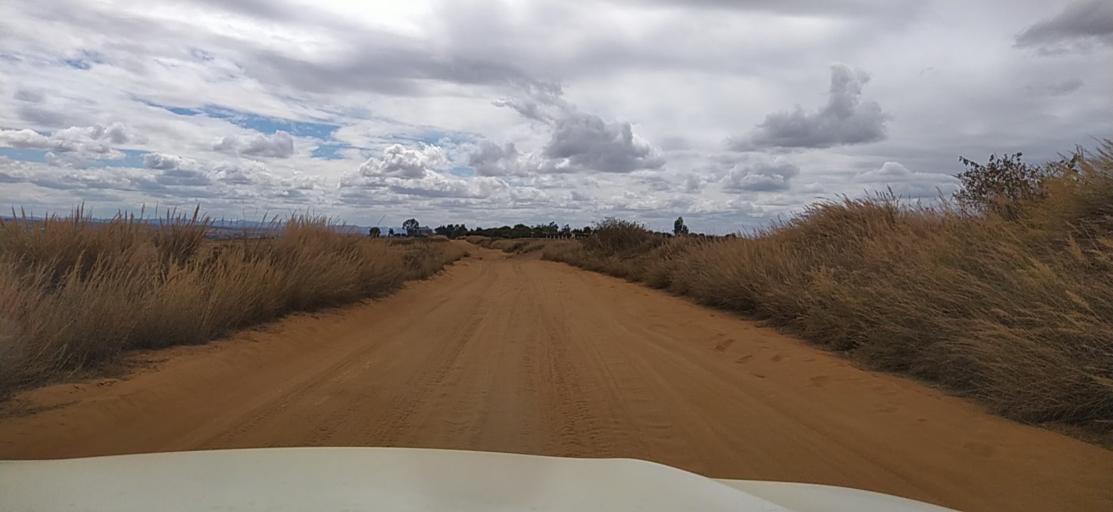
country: MG
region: Alaotra Mangoro
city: Ambatondrazaka
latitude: -17.9040
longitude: 48.2592
